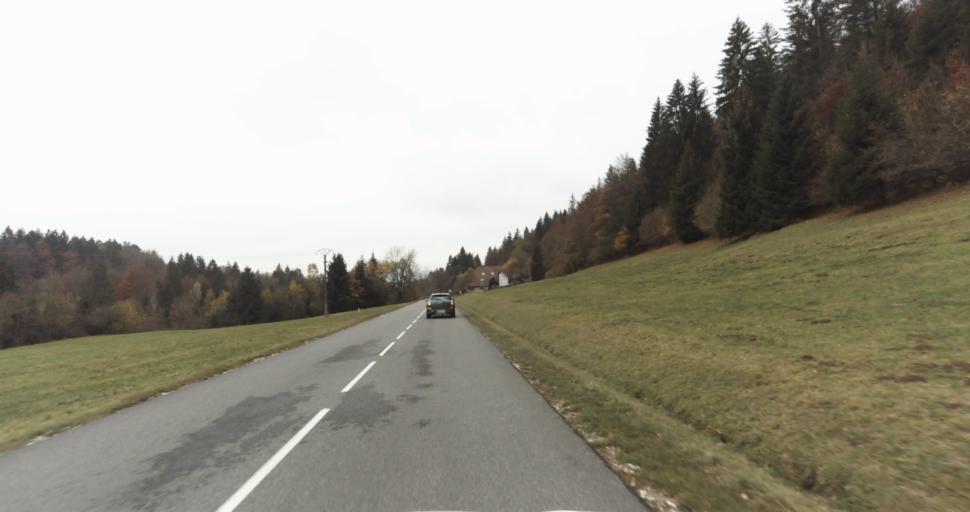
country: FR
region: Rhone-Alpes
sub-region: Departement de la Haute-Savoie
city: Gruffy
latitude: 45.7568
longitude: 6.1175
